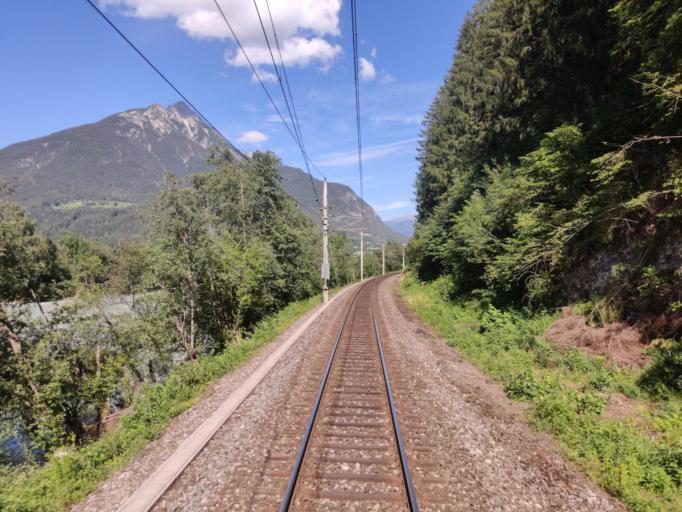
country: AT
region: Tyrol
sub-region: Politischer Bezirk Imst
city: Imst
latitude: 47.2156
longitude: 10.7350
